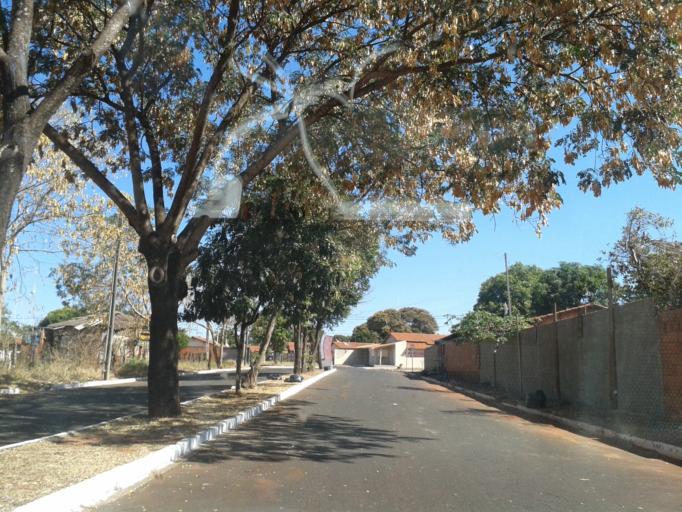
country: BR
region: Minas Gerais
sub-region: Santa Vitoria
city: Santa Vitoria
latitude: -18.8307
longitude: -50.1404
